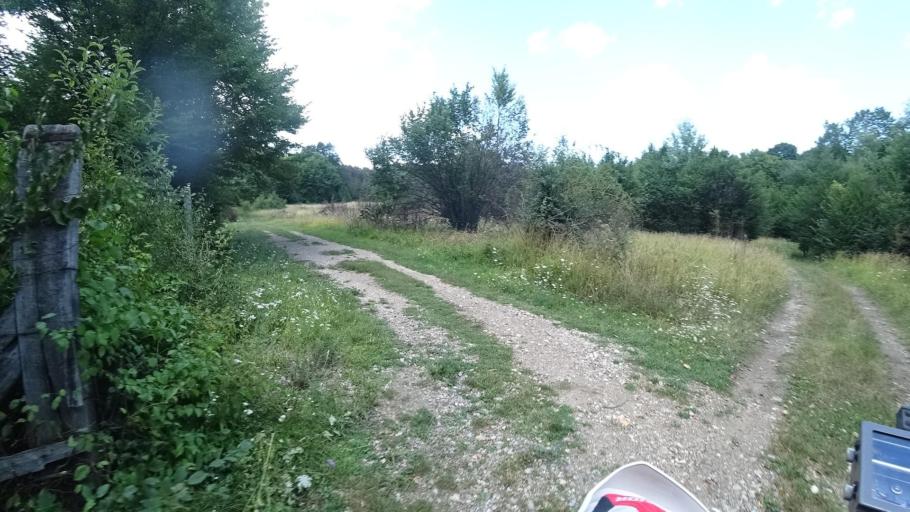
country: HR
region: Karlovacka
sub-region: Grad Ogulin
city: Ogulin
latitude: 45.2532
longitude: 15.1887
